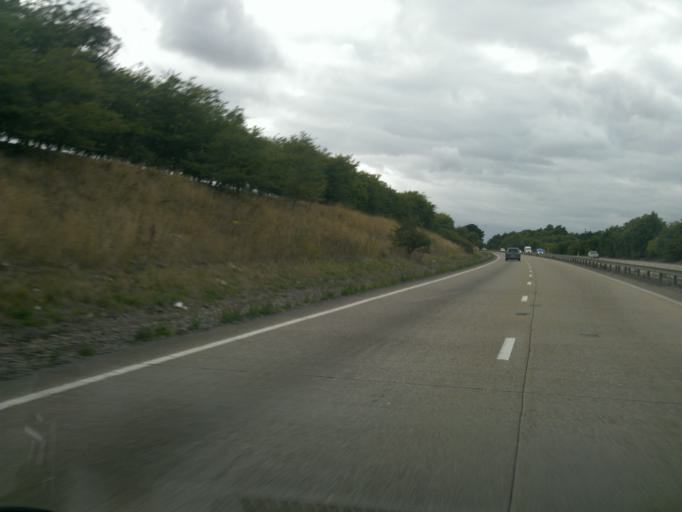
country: GB
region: England
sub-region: Essex
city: Alresford
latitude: 51.8922
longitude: 1.0103
